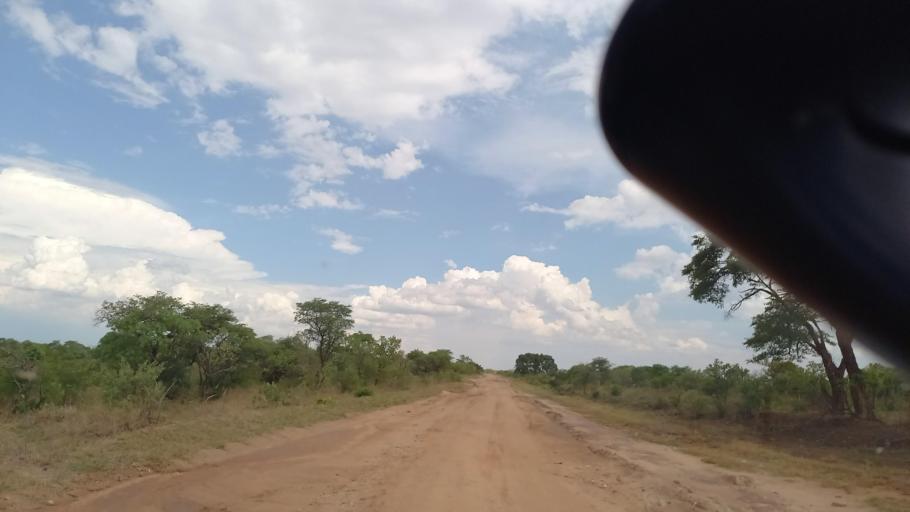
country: ZM
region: Southern
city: Nakambala
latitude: -16.0634
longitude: 27.9952
